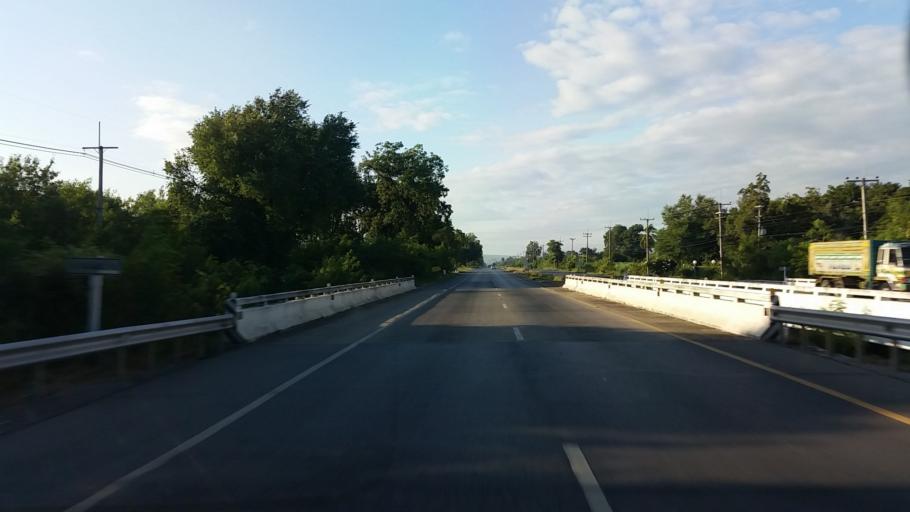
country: TH
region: Lop Buri
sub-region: Amphoe Tha Luang
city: Tha Luang
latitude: 15.0390
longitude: 100.9555
